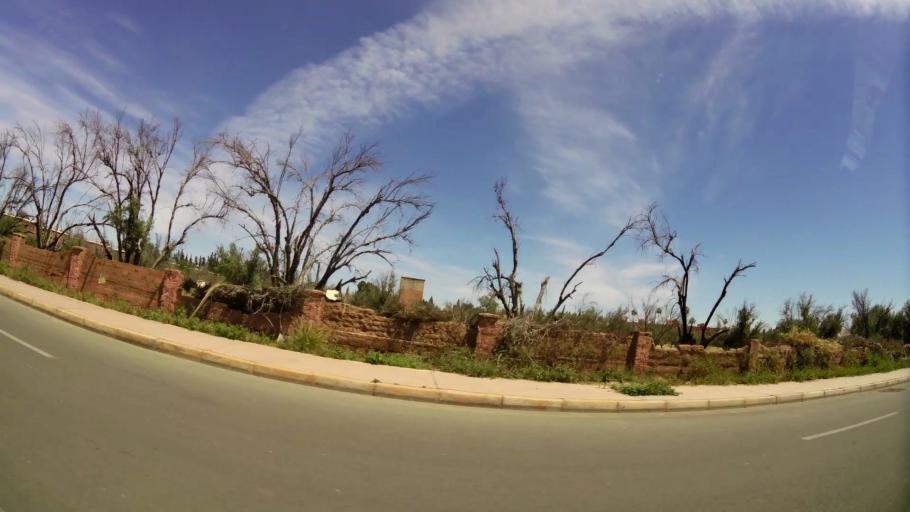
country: MA
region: Marrakech-Tensift-Al Haouz
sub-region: Marrakech
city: Marrakesh
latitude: 31.6483
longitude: -8.0605
